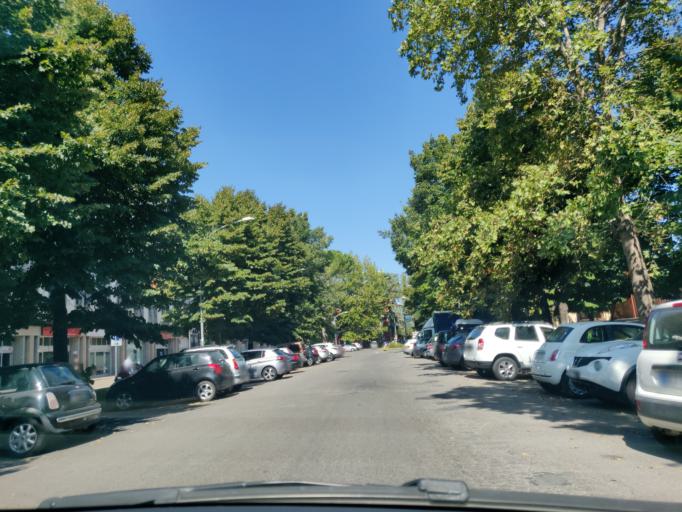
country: IT
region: Latium
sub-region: Provincia di Viterbo
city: Viterbo
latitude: 42.4242
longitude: 12.1063
